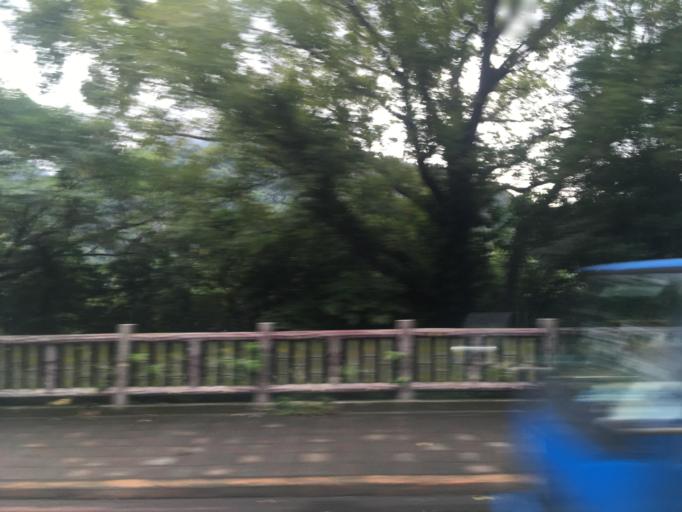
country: TW
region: Taipei
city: Taipei
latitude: 25.1431
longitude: 121.5273
